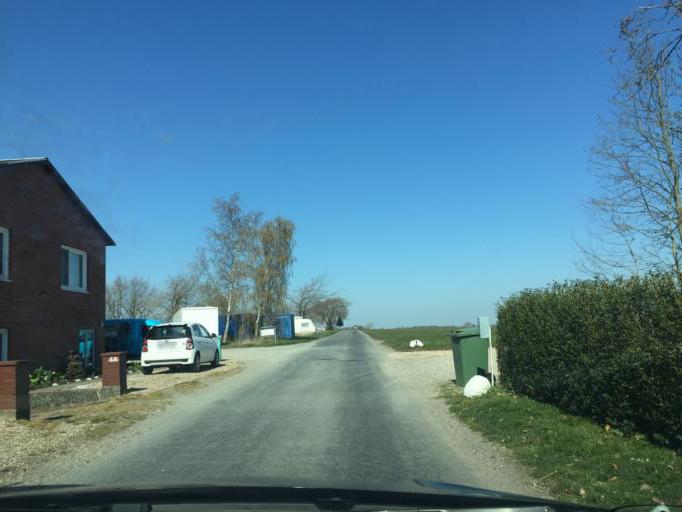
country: DK
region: South Denmark
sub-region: Faaborg-Midtfyn Kommune
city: Arslev
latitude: 55.2867
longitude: 10.5310
